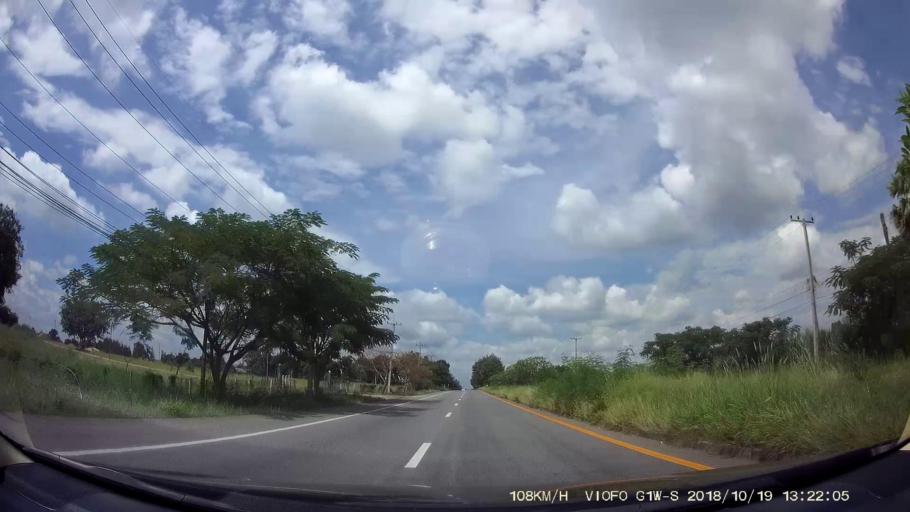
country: TH
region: Chaiyaphum
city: Chatturat
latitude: 15.4717
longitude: 101.8245
